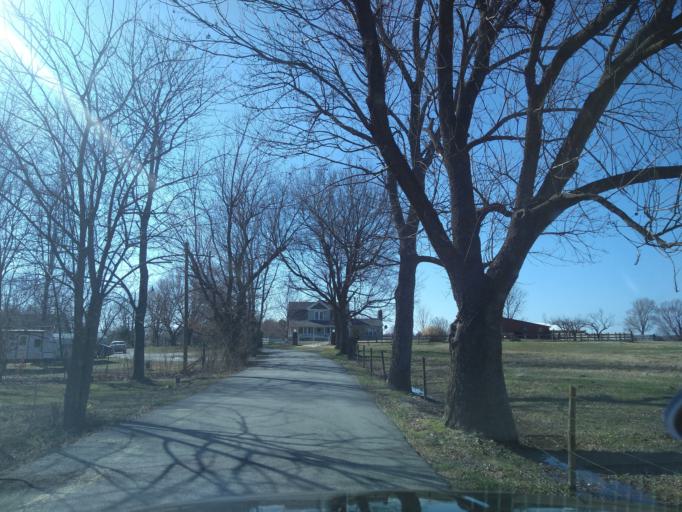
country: US
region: Arkansas
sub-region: Washington County
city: Farmington
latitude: 36.0680
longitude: -94.2404
